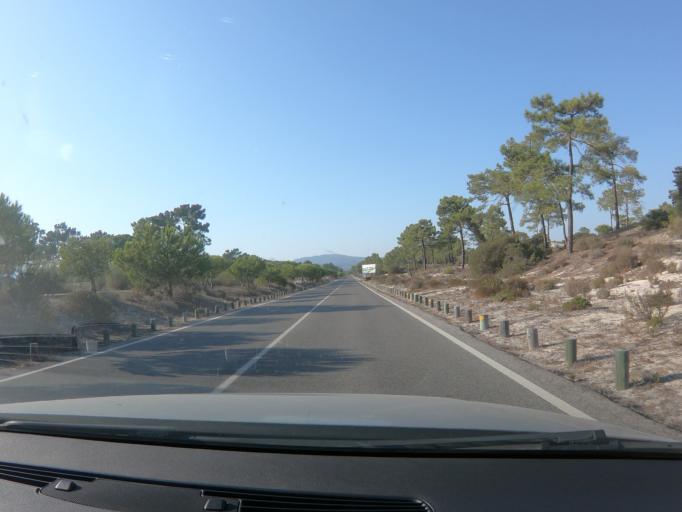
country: PT
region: Setubal
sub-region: Setubal
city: Setubal
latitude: 38.4778
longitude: -8.8882
